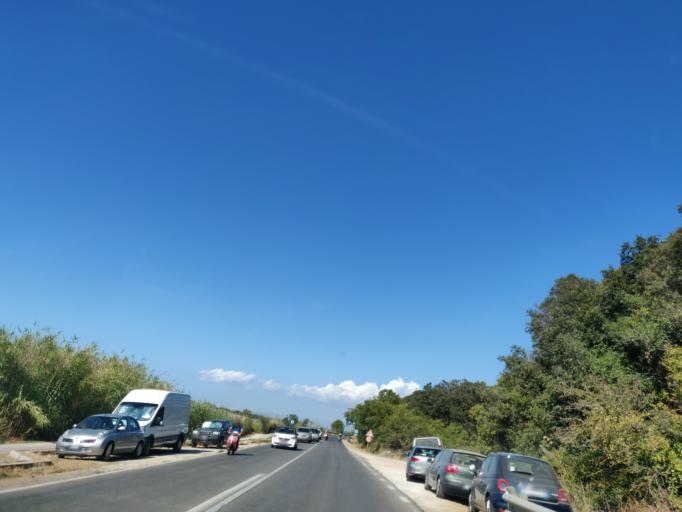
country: IT
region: Tuscany
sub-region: Provincia di Grosseto
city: Porto Ercole
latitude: 42.4308
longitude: 11.1701
